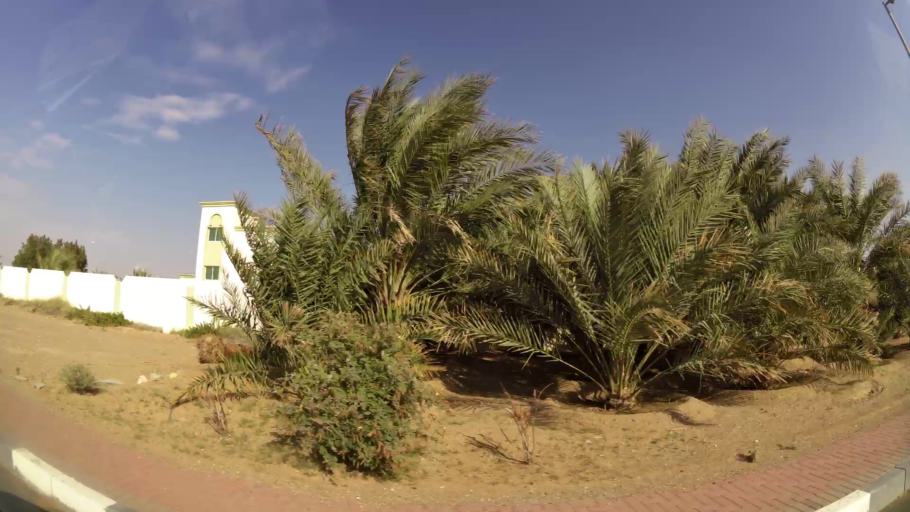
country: AE
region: Abu Dhabi
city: Al Ain
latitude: 24.0738
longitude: 55.8609
